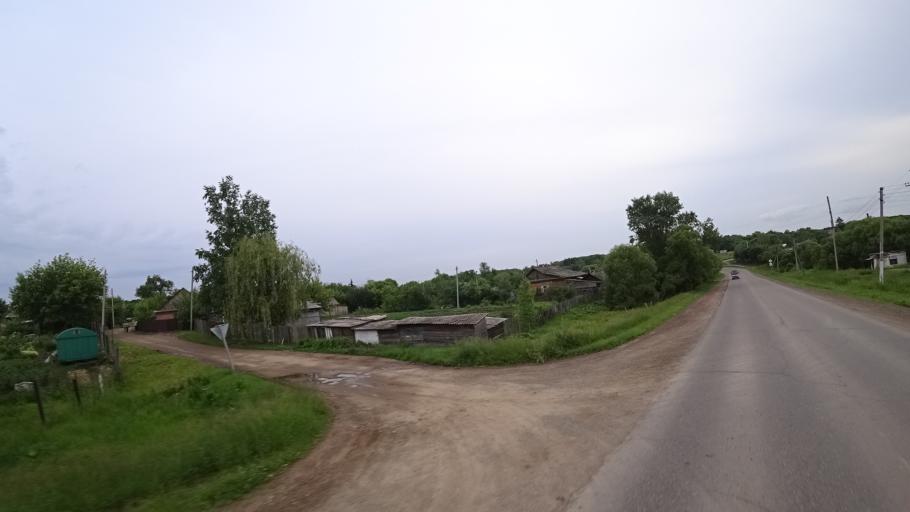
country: RU
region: Primorskiy
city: Novosysoyevka
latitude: 44.2278
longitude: 133.3537
